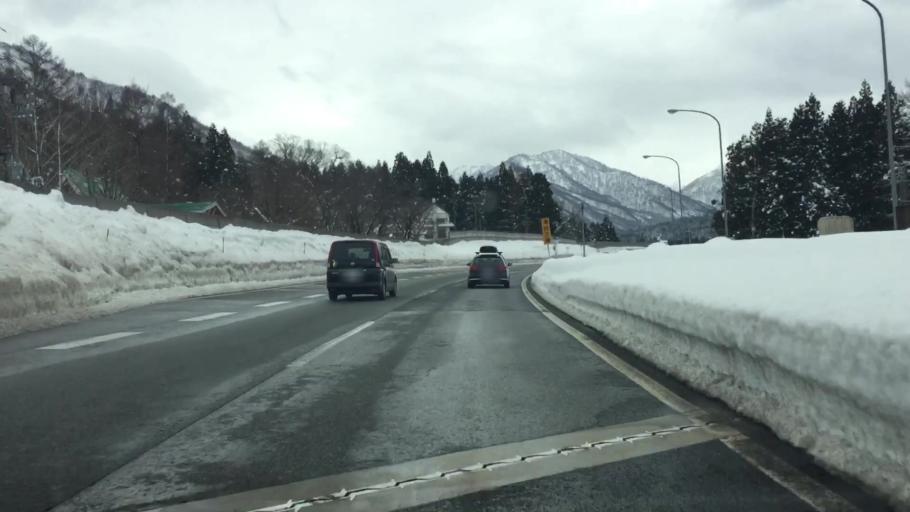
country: JP
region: Niigata
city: Shiozawa
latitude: 36.9040
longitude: 138.8474
